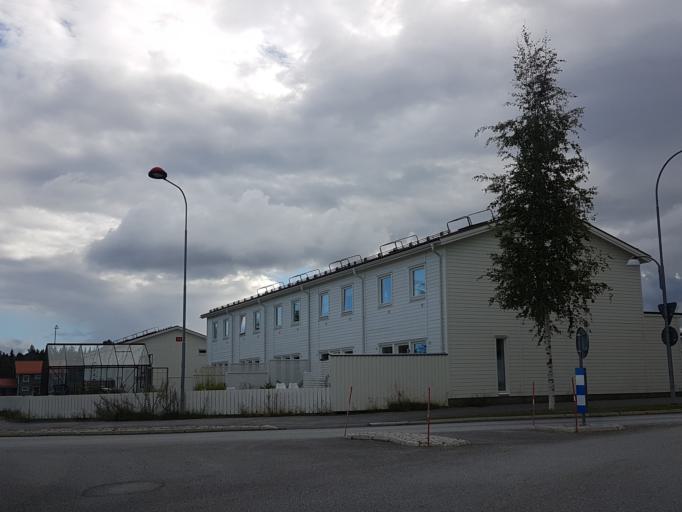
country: SE
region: Vaesterbotten
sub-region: Umea Kommun
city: Ersmark
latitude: 63.8029
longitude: 20.3693
